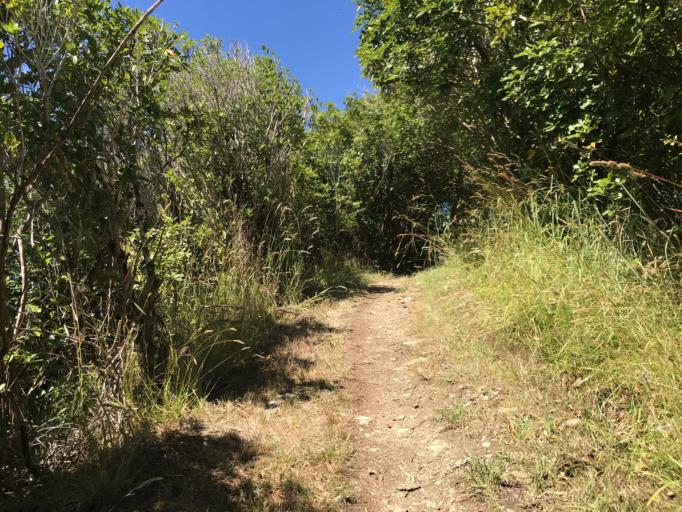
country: NZ
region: Marlborough
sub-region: Marlborough District
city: Picton
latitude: -41.2062
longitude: 174.0240
